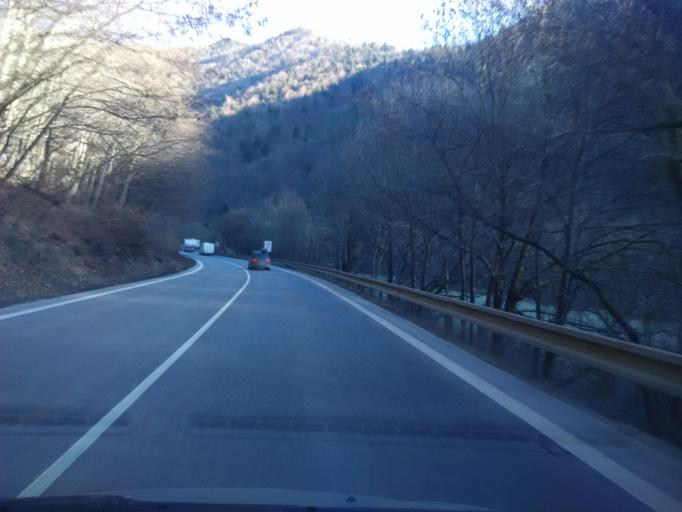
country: SK
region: Zilinsky
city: Krasnany
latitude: 49.1660
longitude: 18.8860
